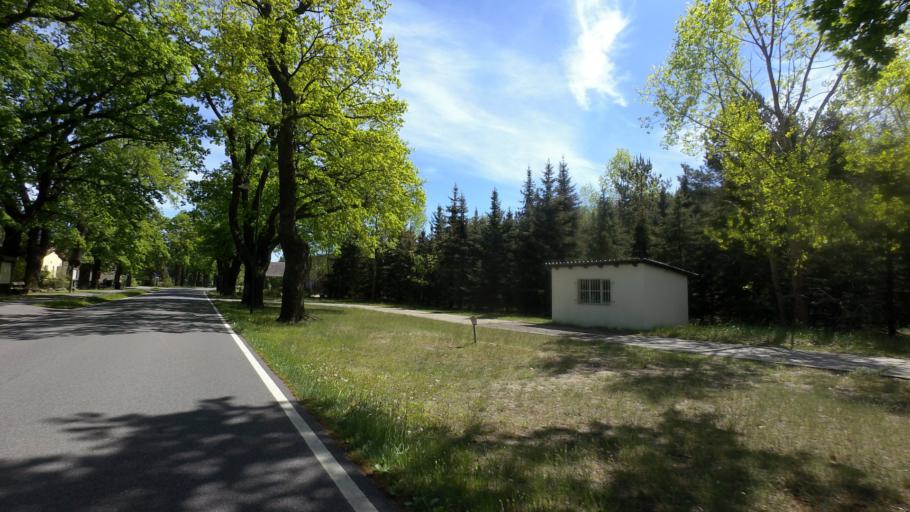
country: DE
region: Brandenburg
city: Luckenwalde
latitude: 52.0485
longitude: 13.2781
